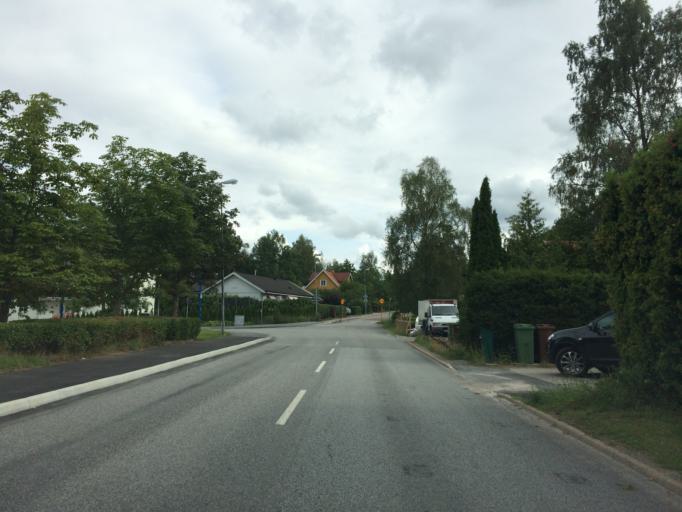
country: SE
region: Stockholm
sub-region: Sollentuna Kommun
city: Sollentuna
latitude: 59.4560
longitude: 17.8935
